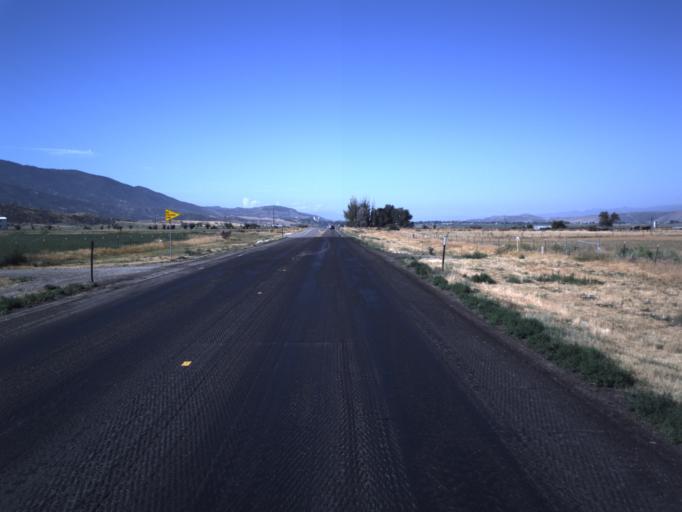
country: US
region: Utah
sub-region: Sanpete County
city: Ephraim
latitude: 39.3341
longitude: -111.5980
